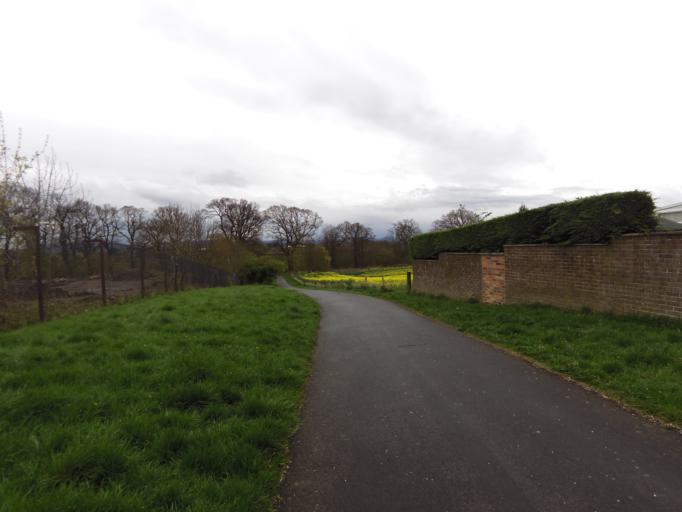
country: GB
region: Scotland
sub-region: Edinburgh
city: Queensferry
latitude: 55.9812
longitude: -3.3824
